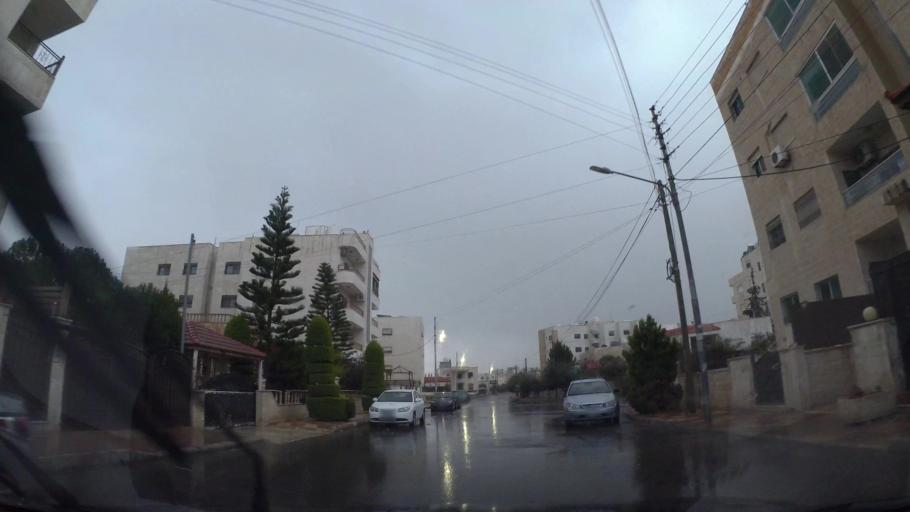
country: JO
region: Amman
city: Amman
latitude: 32.0023
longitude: 35.9547
